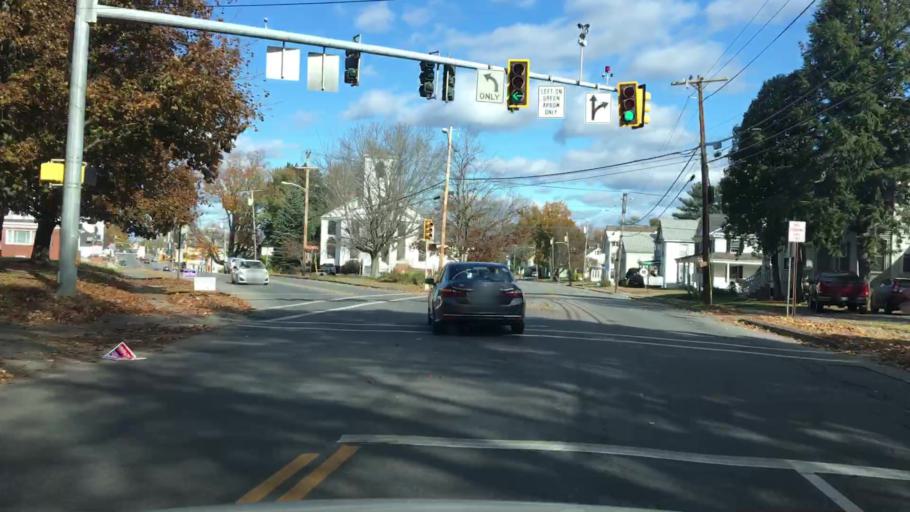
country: US
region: Maine
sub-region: Kennebec County
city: Waterville
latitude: 44.5459
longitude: -69.6363
